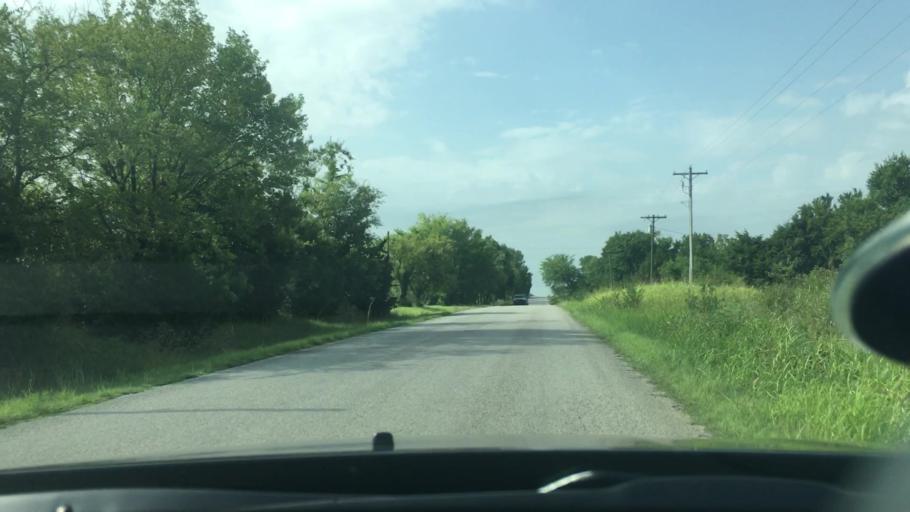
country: US
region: Oklahoma
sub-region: Carter County
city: Lone Grove
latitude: 34.2061
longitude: -97.2650
